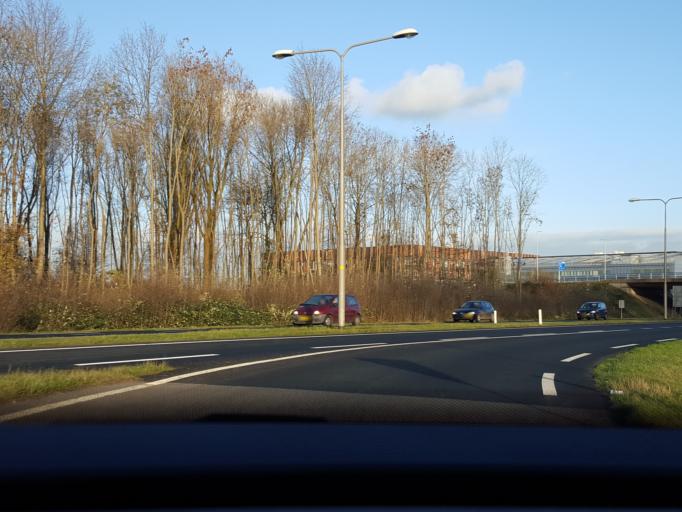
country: NL
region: Gelderland
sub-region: Gemeente Zutphen
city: Leesten
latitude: 52.1215
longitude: 6.2136
